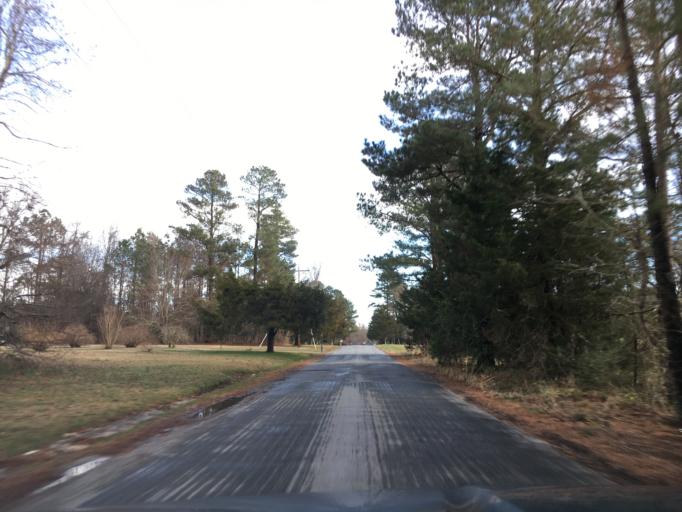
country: US
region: Virginia
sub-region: Nottoway County
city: Crewe
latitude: 37.2373
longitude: -78.2381
